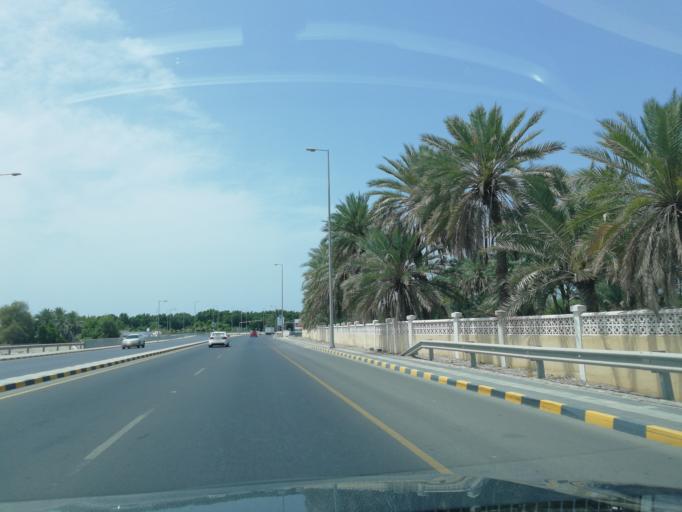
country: OM
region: Muhafazat Masqat
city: As Sib al Jadidah
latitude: 23.6689
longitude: 58.1921
